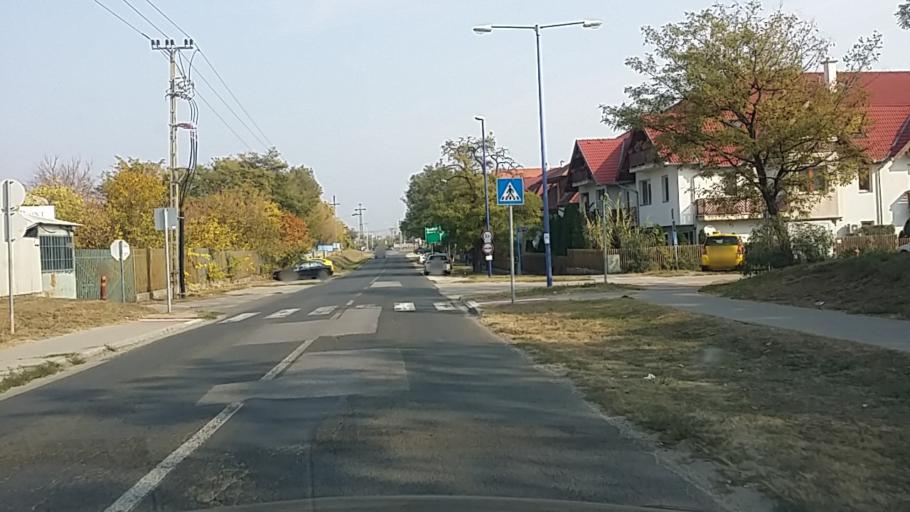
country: HU
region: Pest
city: Dunakeszi
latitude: 47.6206
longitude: 19.1571
